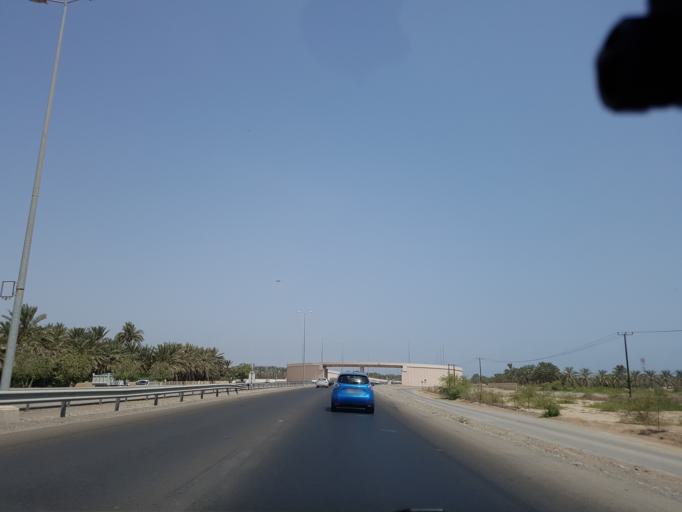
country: OM
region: Al Batinah
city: Saham
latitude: 24.1780
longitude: 56.8572
